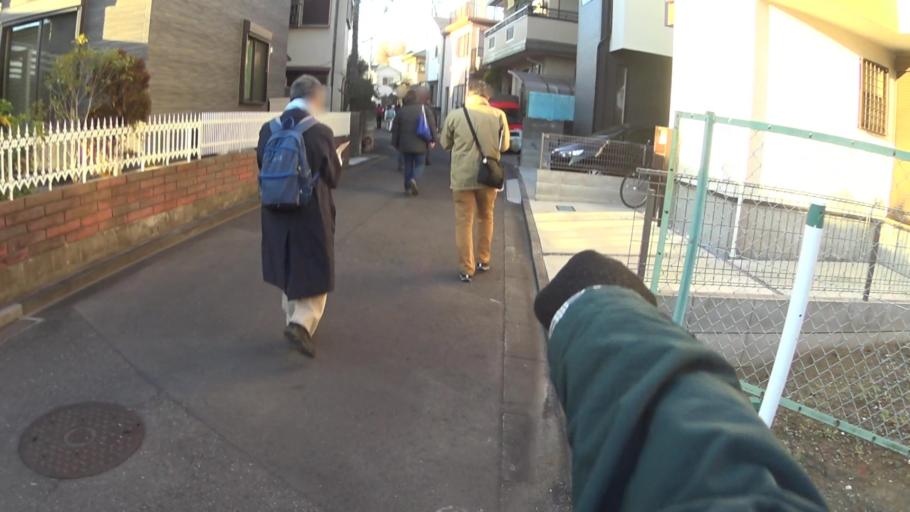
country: JP
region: Saitama
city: Shimotoda
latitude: 35.8508
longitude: 139.6846
